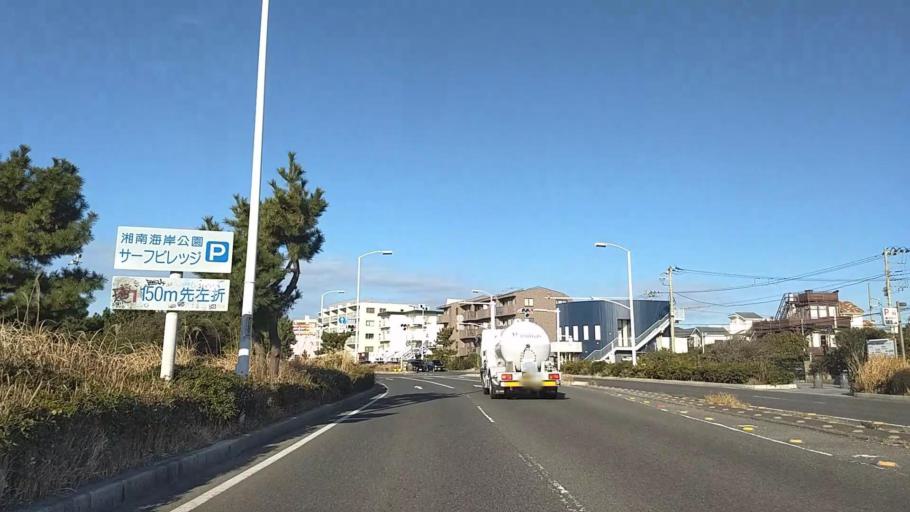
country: JP
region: Kanagawa
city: Fujisawa
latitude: 35.3166
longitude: 139.4714
